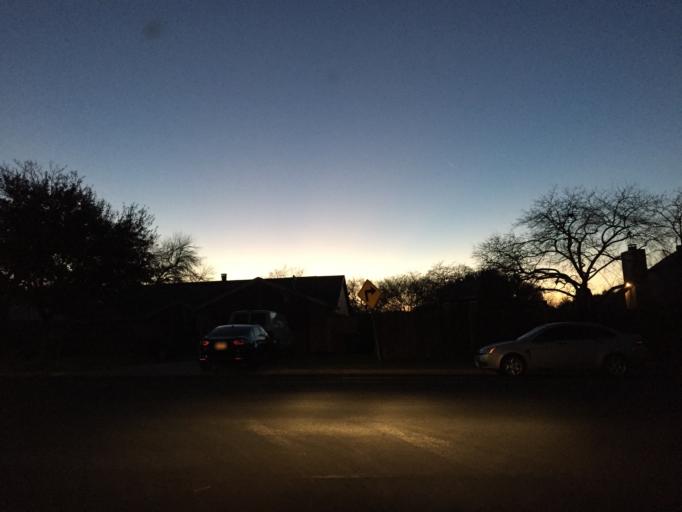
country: US
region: Texas
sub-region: Travis County
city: Wells Branch
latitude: 30.3878
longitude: -97.6943
